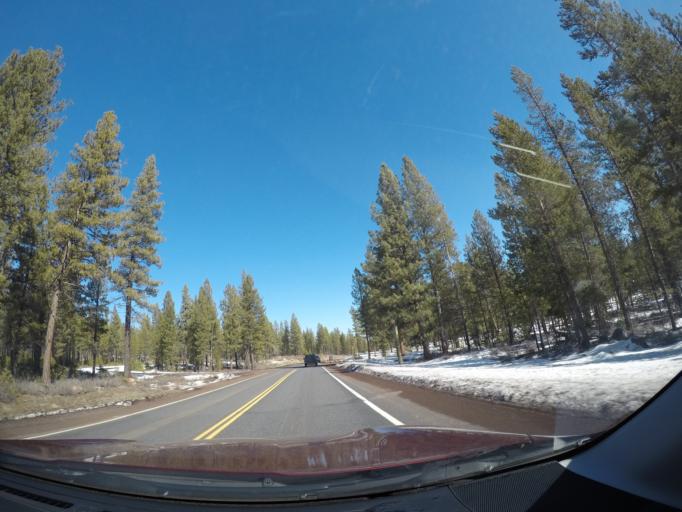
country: US
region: Oregon
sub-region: Deschutes County
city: Three Rivers
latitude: 43.8619
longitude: -121.4890
